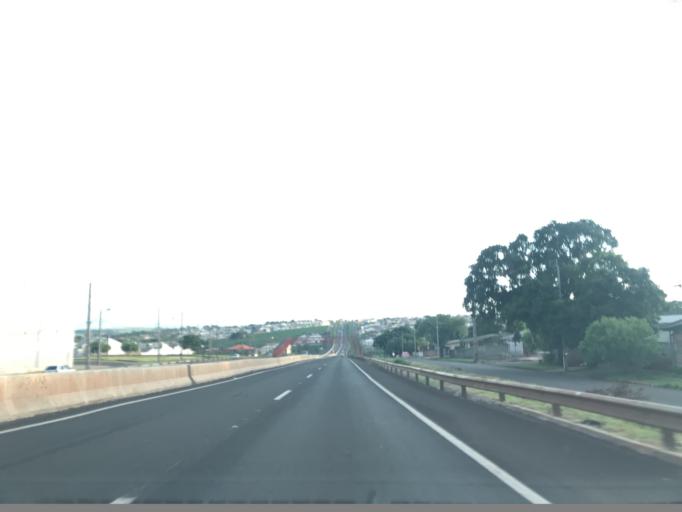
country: BR
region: Parana
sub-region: Maringa
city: Maringa
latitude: -23.3926
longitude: -51.9715
